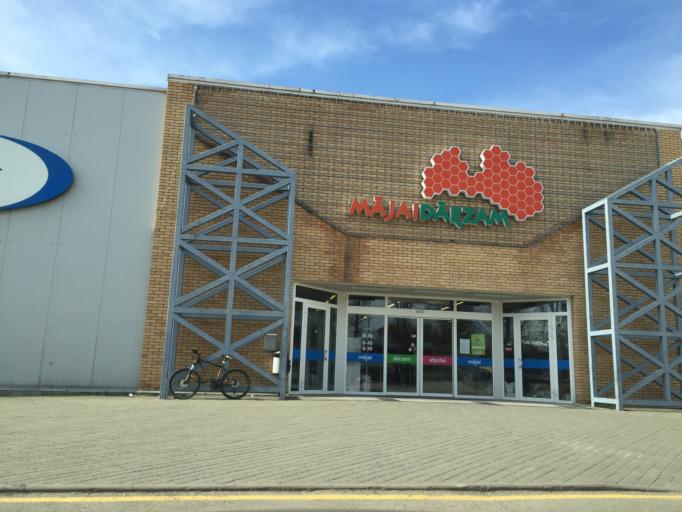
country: LV
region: Ogre
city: Ogre
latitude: 56.8165
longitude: 24.5981
